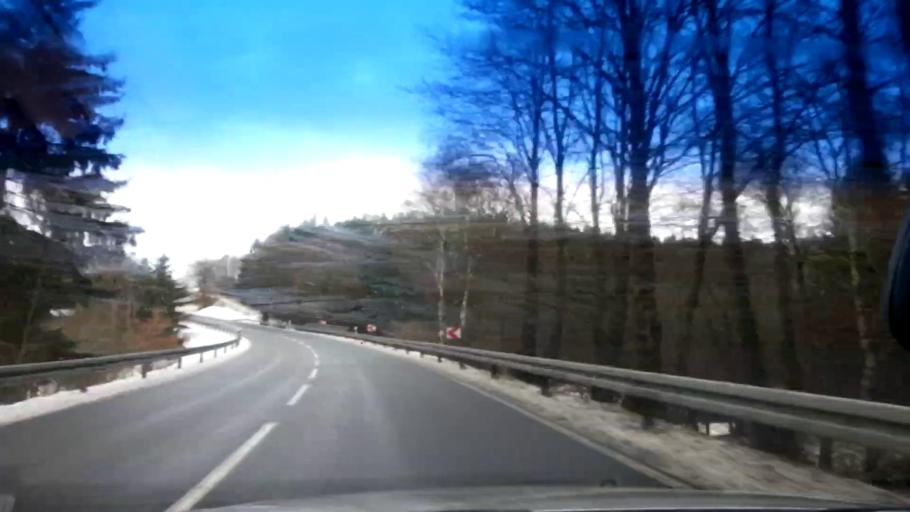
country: DE
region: Bavaria
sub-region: Upper Franconia
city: Marktleuthen
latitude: 50.1418
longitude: 12.0168
